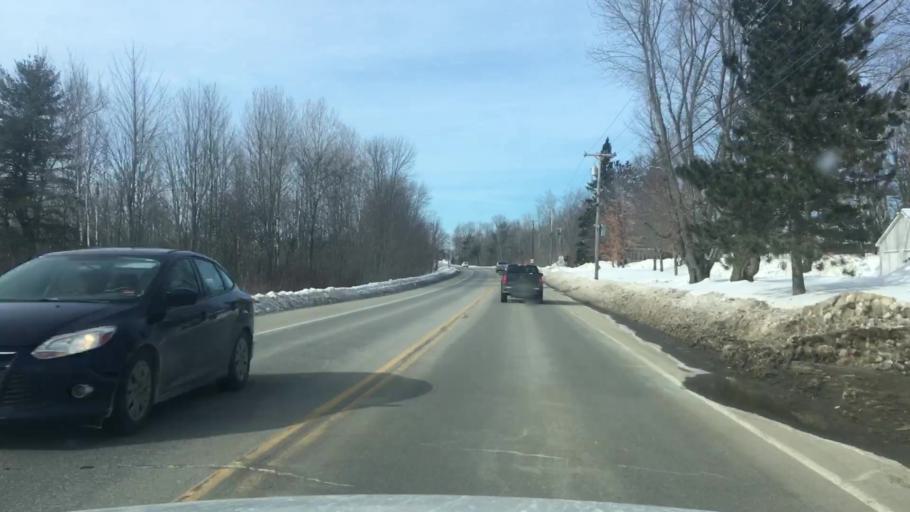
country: US
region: Maine
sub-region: Penobscot County
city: Kenduskeag
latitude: 44.9270
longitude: -68.9342
